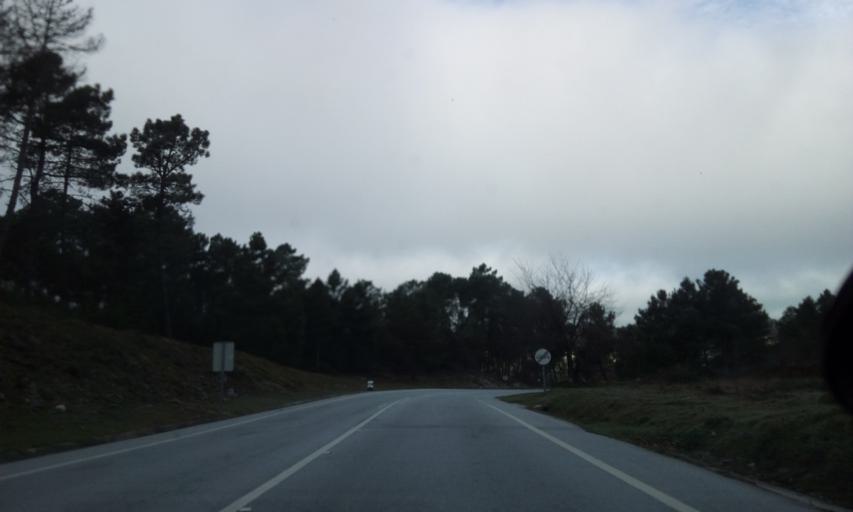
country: PT
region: Guarda
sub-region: Aguiar da Beira
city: Aguiar da Beira
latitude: 40.7441
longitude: -7.4997
